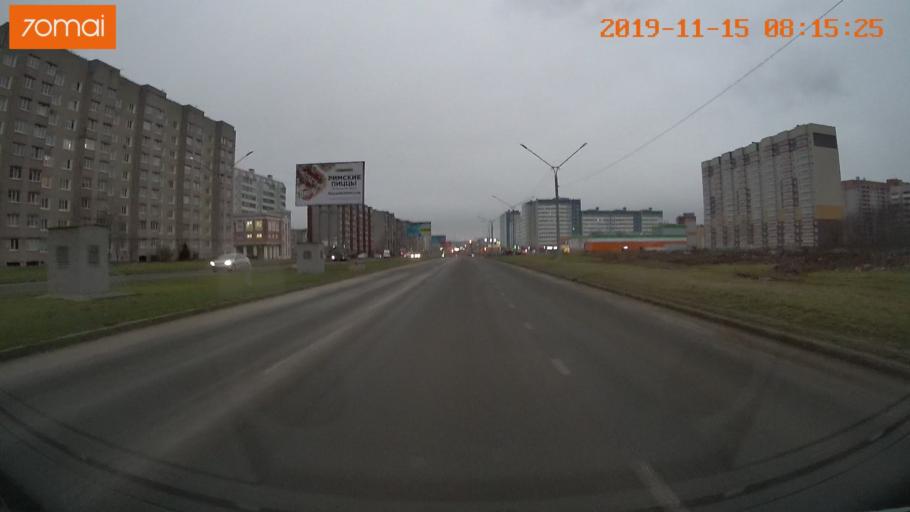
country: RU
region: Vologda
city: Cherepovets
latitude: 59.0821
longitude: 37.9225
